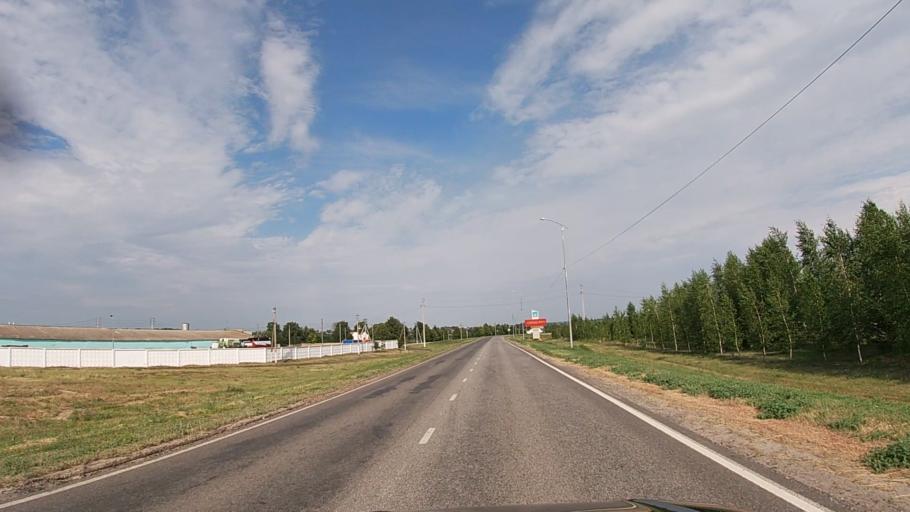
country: RU
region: Belgorod
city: Krasnaya Yaruga
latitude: 50.7981
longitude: 35.6825
